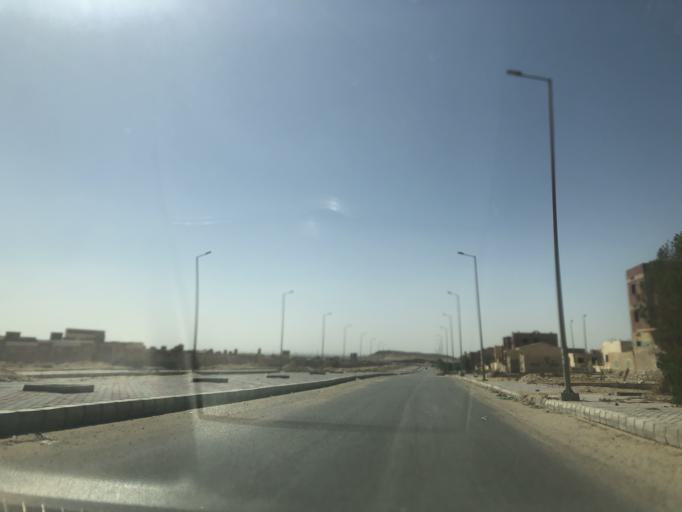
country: EG
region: Al Jizah
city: Madinat Sittah Uktubar
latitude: 29.9311
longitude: 30.9645
